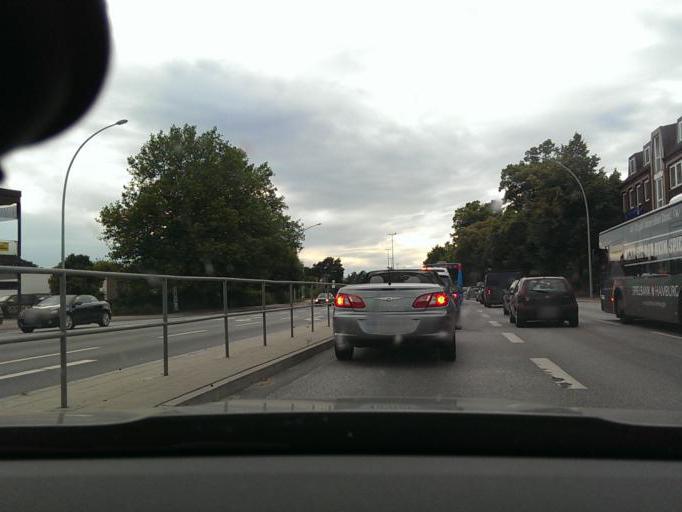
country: DE
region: Hamburg
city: Stellingen
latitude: 53.5931
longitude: 9.9276
